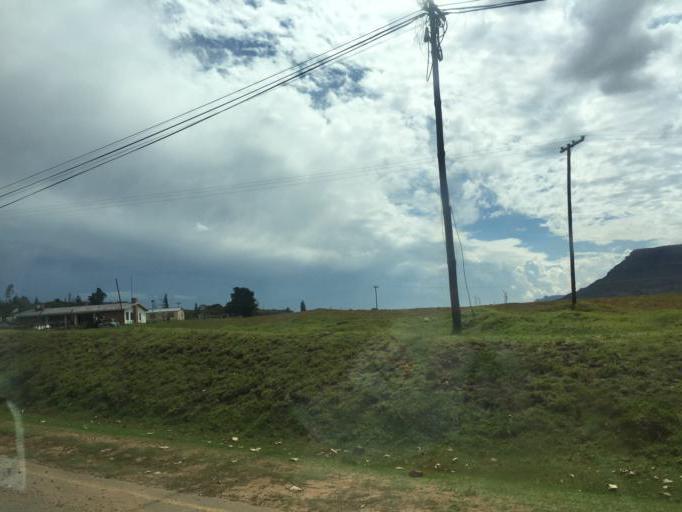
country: LS
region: Maseru
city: Nako
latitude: -29.6265
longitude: 27.5031
